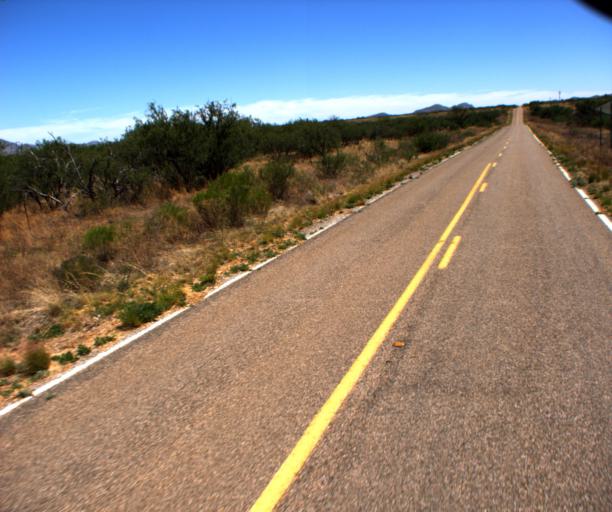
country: US
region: Arizona
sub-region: Santa Cruz County
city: Tubac
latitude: 31.5468
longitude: -111.5400
